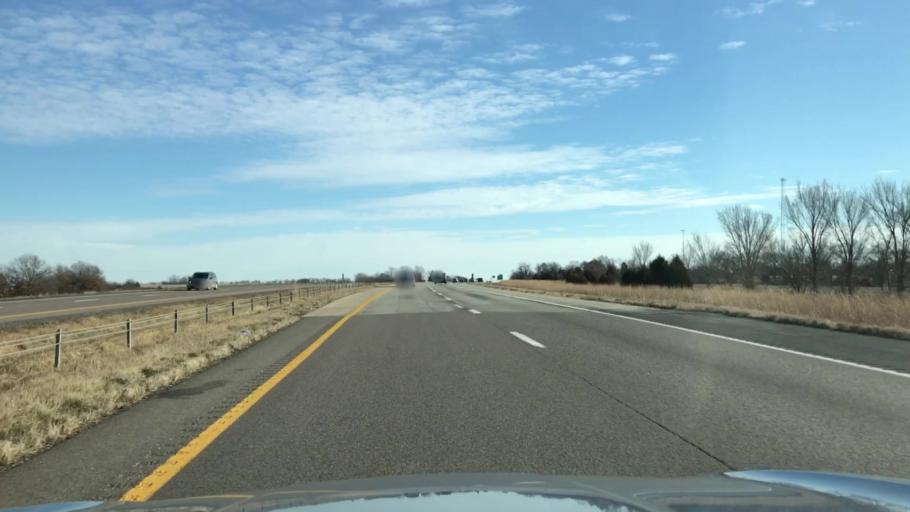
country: US
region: Missouri
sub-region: Callaway County
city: Fulton
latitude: 38.9376
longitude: -91.8205
